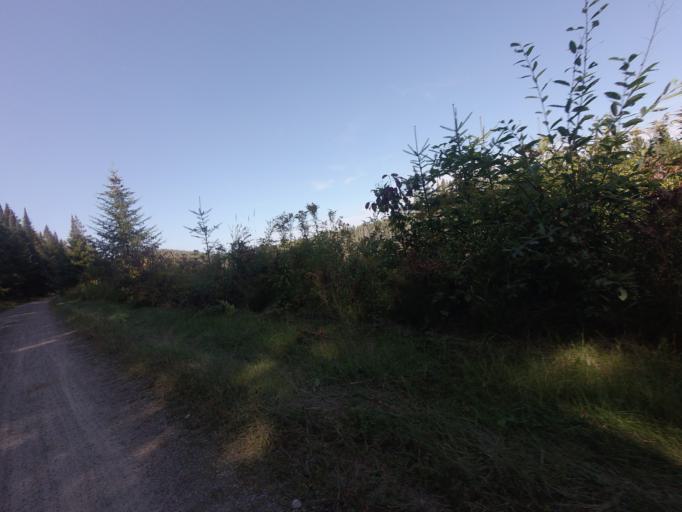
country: CA
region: Quebec
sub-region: Laurentides
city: Sainte-Agathe-des-Monts
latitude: 46.0839
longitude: -74.3368
